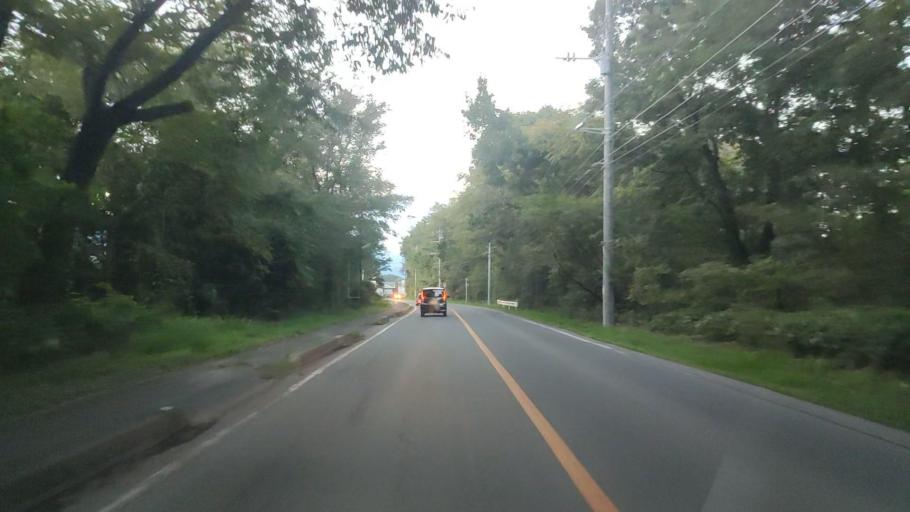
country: JP
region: Nagano
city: Komoro
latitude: 36.4952
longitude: 138.5848
